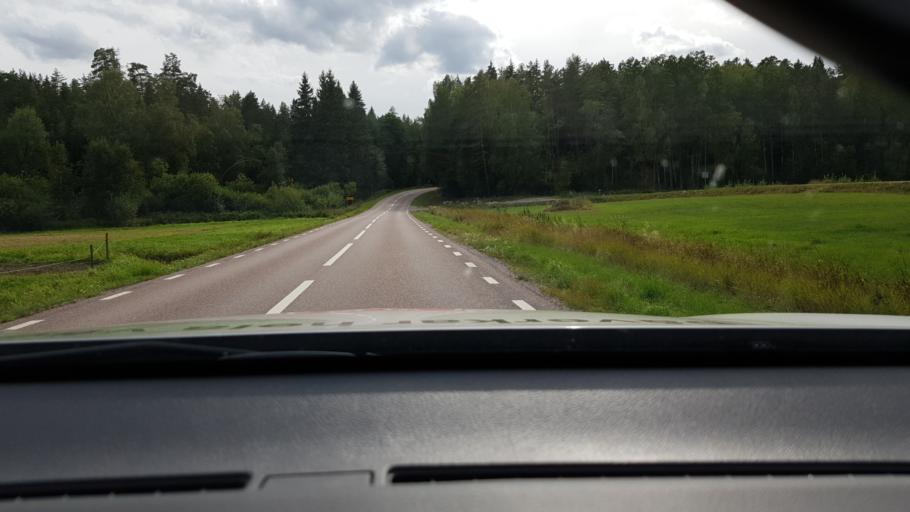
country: SE
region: Soedermanland
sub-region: Gnesta Kommun
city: Gnesta
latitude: 58.9939
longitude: 17.1675
